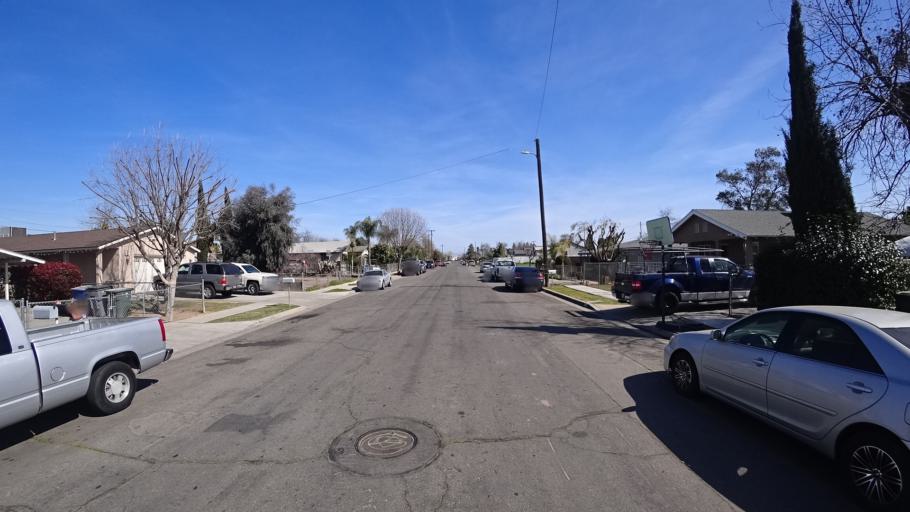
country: US
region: California
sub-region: Fresno County
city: Clovis
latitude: 36.8435
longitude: -119.7963
